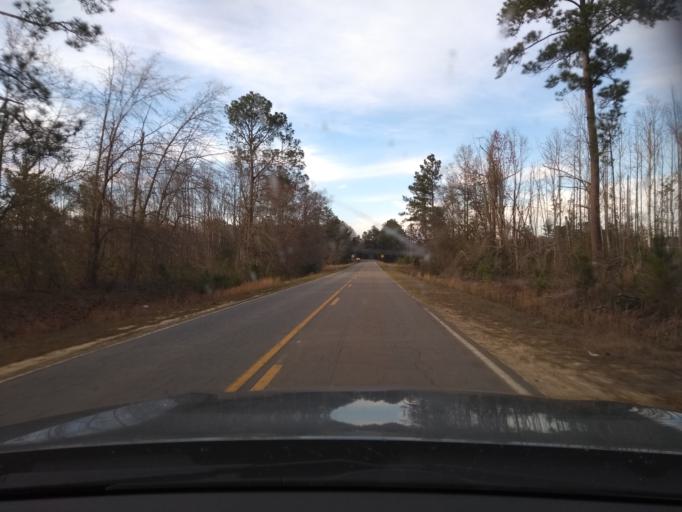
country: US
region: Georgia
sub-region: Evans County
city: Claxton
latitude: 32.2205
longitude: -81.7687
